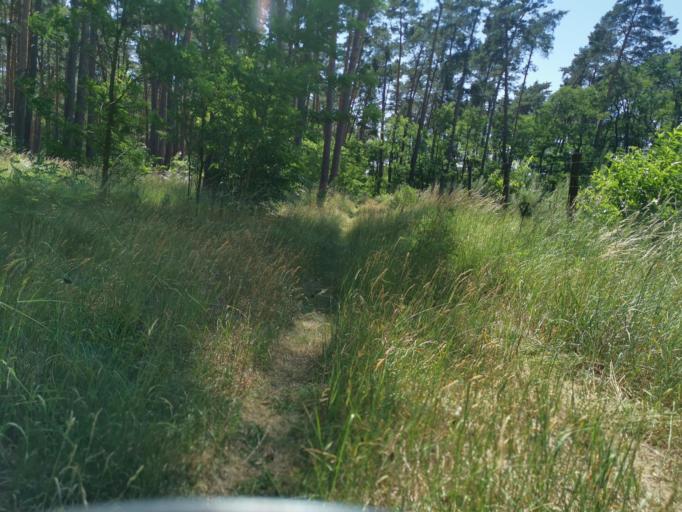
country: CZ
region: South Moravian
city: Rohatec
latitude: 48.9097
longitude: 17.2189
